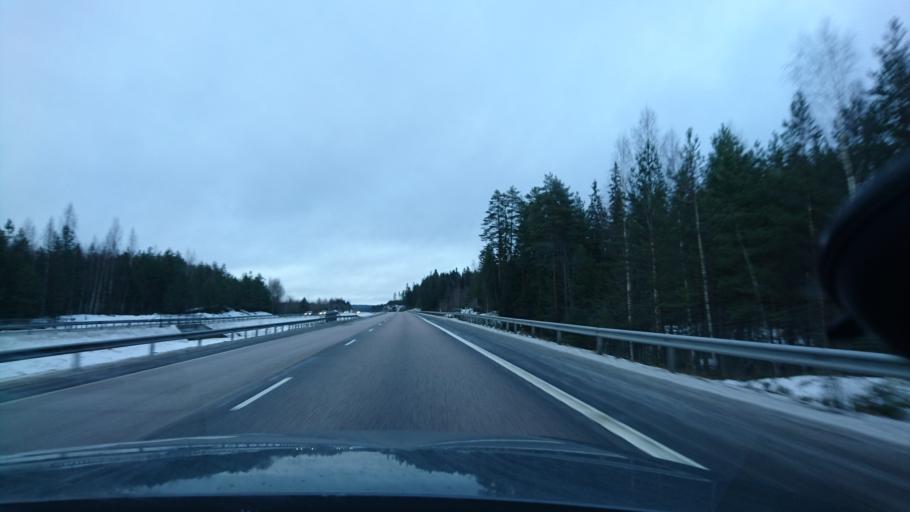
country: FI
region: Uusimaa
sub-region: Porvoo
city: Pukkila
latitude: 60.7446
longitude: 25.4554
